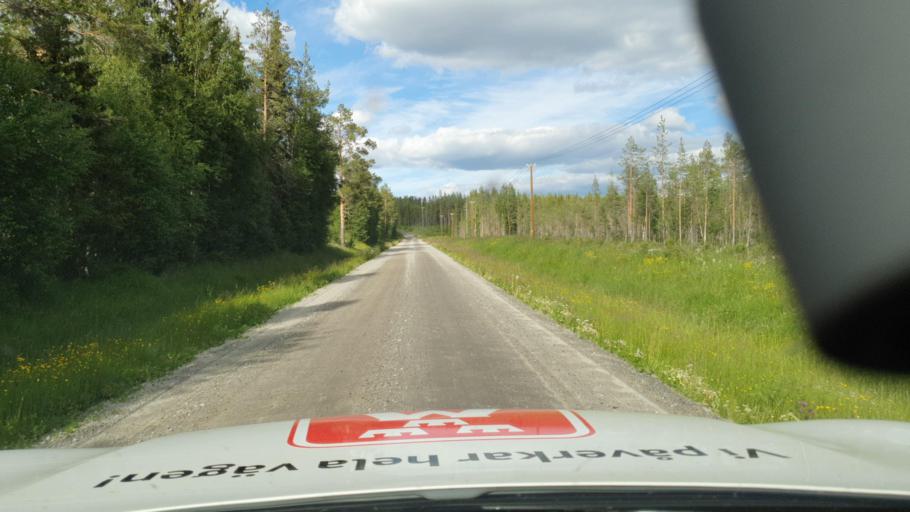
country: SE
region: Vaesterbotten
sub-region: Lycksele Kommun
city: Soderfors
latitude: 64.2807
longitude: 18.1612
